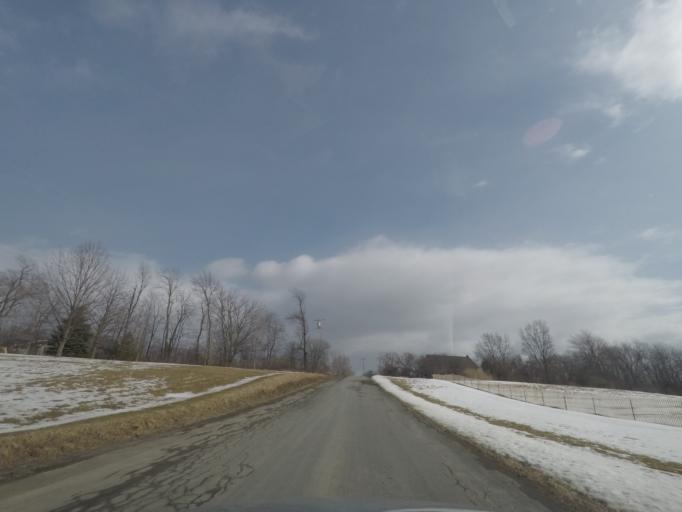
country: US
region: New York
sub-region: Rensselaer County
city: Poestenkill
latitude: 42.7800
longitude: -73.5568
